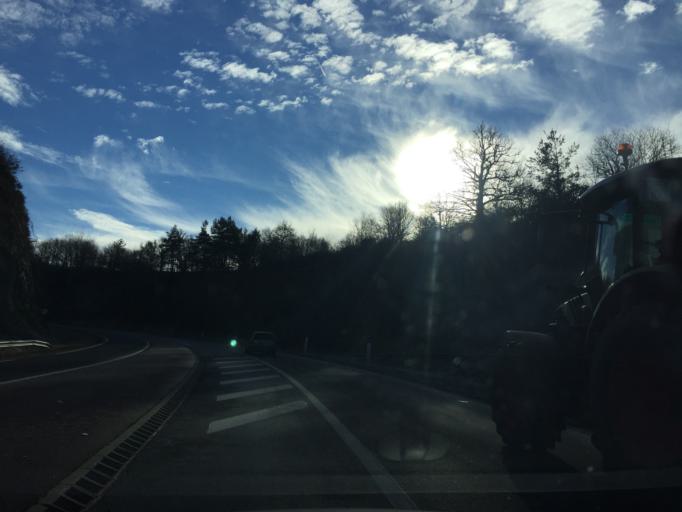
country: FR
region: Auvergne
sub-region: Departement du Puy-de-Dome
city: Gelles
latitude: 45.8564
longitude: 2.6698
